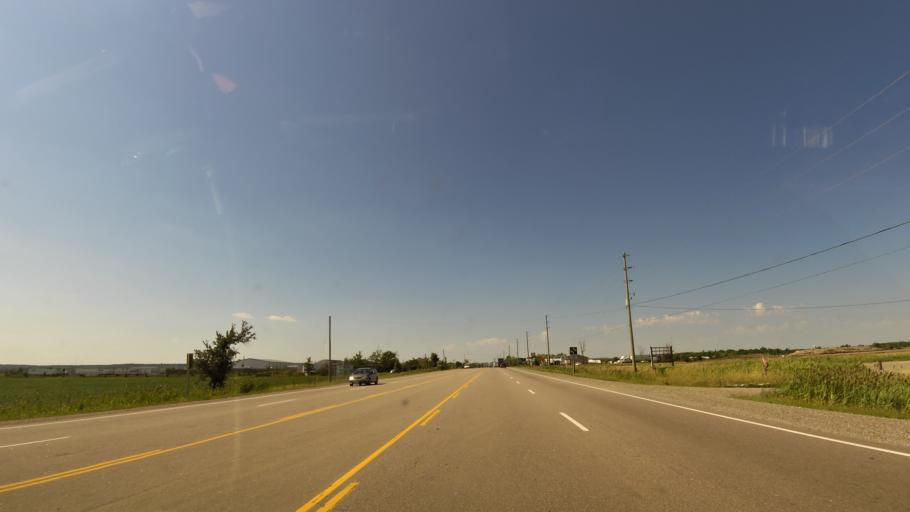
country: CA
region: Ontario
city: Brampton
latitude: 43.7680
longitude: -79.8708
